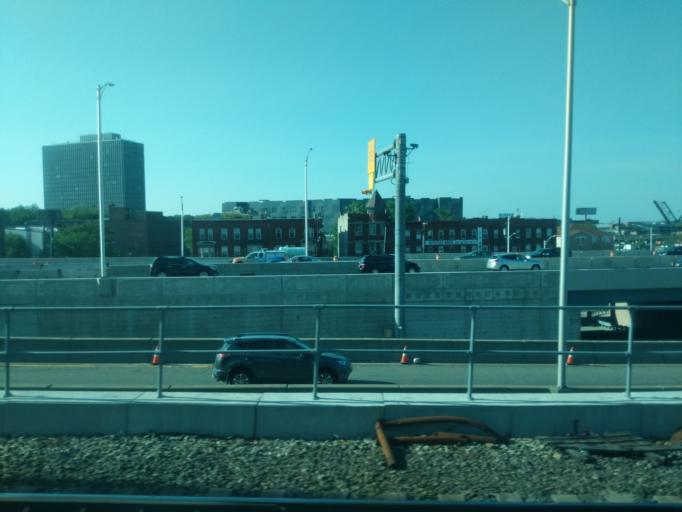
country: US
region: New Jersey
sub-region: Hudson County
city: East Newark
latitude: 40.7475
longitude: -74.1693
